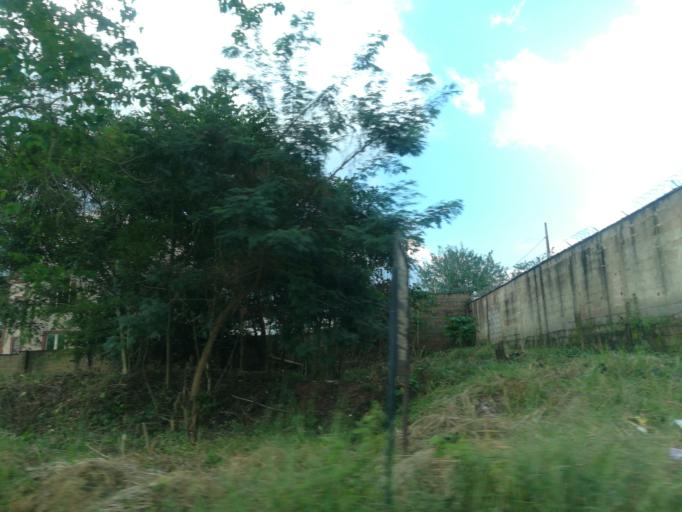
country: NG
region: Oyo
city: Ibadan
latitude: 7.4007
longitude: 3.8392
